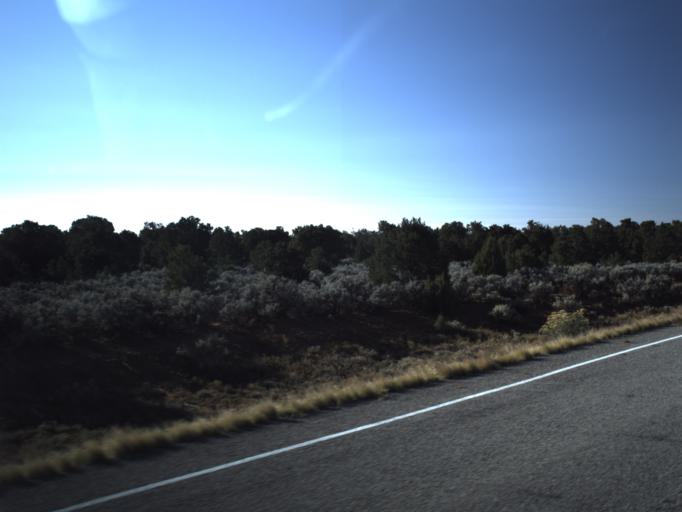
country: US
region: Utah
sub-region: San Juan County
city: Blanding
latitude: 37.5648
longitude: -109.9281
